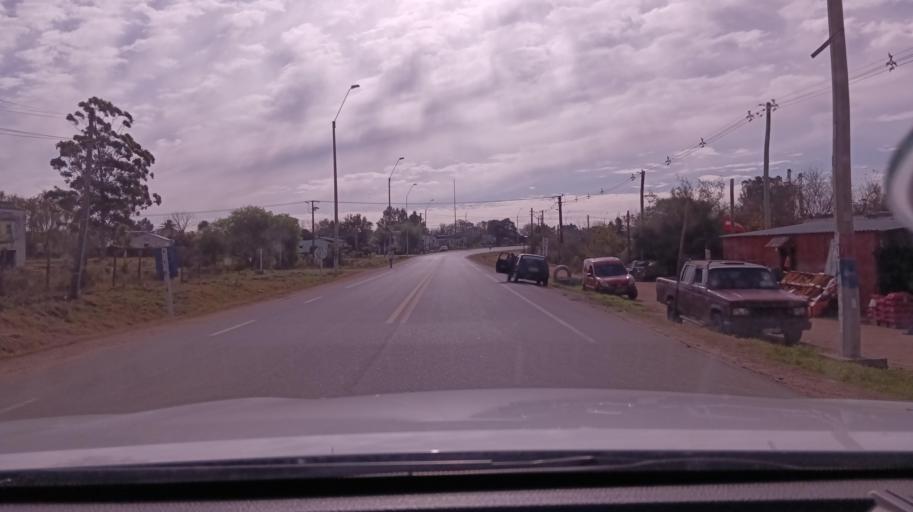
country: UY
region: Canelones
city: Toledo
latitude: -34.7371
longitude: -56.1139
